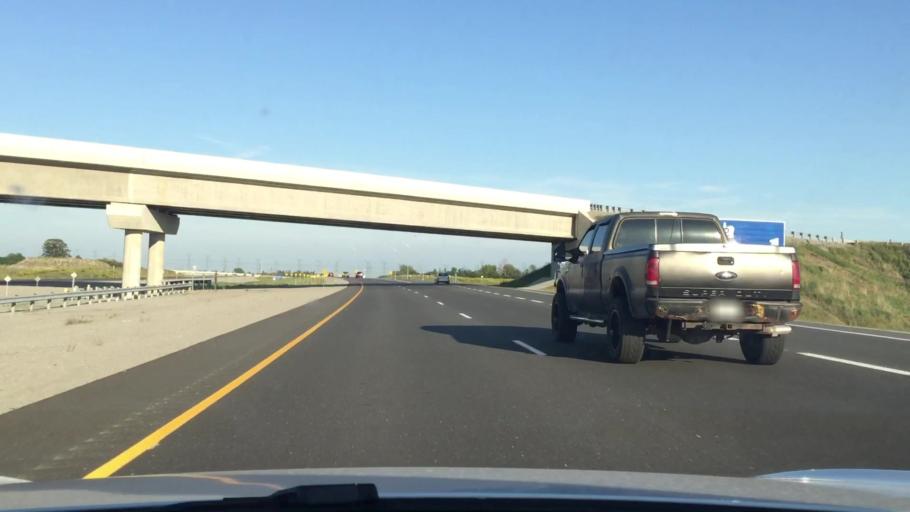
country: CA
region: Ontario
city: Ajax
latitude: 43.9487
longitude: -78.9723
